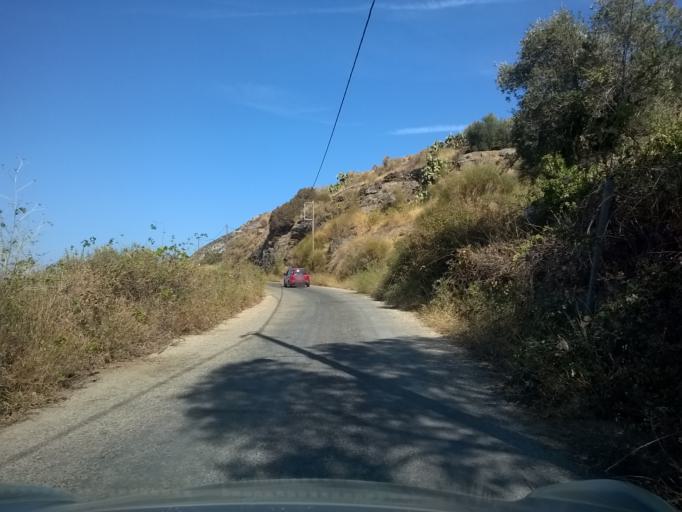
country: GR
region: South Aegean
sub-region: Nomos Kykladon
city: Filotion
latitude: 37.1643
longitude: 25.5458
